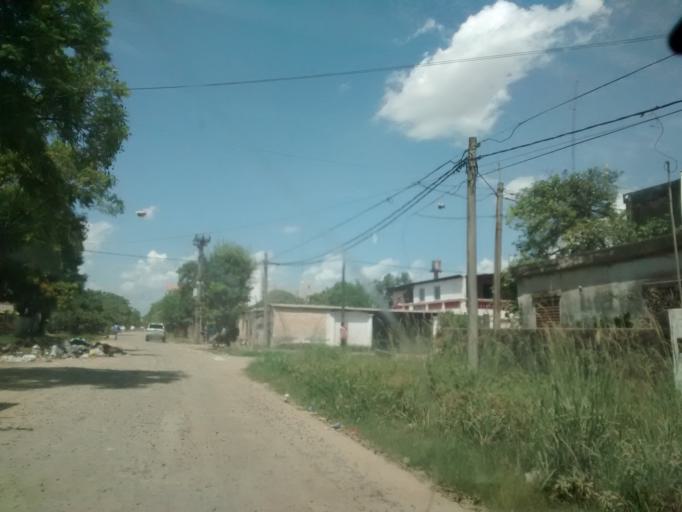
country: AR
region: Chaco
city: Resistencia
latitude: -27.4493
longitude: -58.9703
